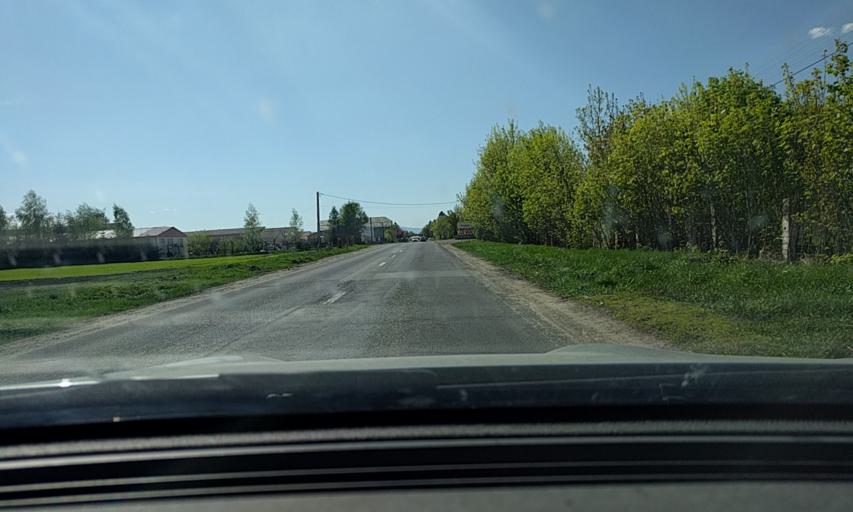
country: RO
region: Brasov
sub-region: Comuna Prejmer
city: Prejmer
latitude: 45.7138
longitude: 25.7858
